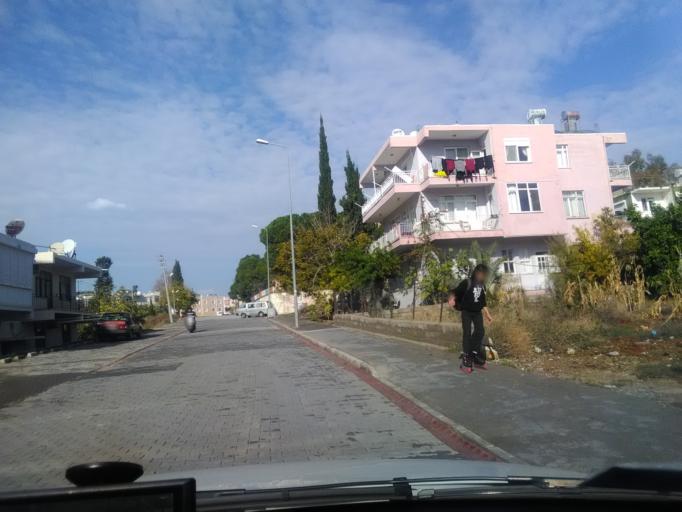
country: TR
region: Antalya
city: Gazipasa
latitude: 36.2701
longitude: 32.3095
